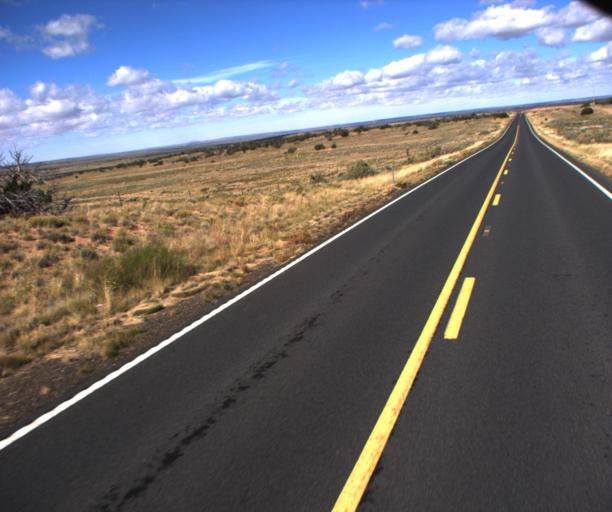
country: US
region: Arizona
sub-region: Apache County
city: Houck
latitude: 35.0778
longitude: -109.2988
